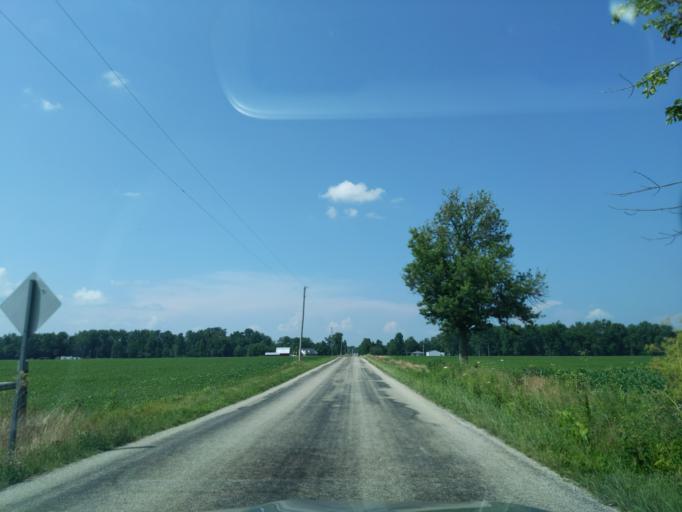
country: US
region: Indiana
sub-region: Ripley County
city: Osgood
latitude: 39.0775
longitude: -85.3484
